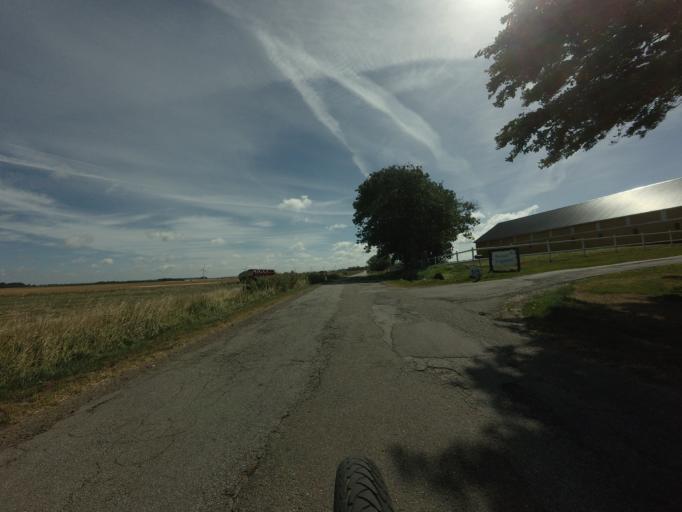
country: DK
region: North Denmark
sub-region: Hjorring Kommune
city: Vra
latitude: 57.3420
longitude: 9.7978
